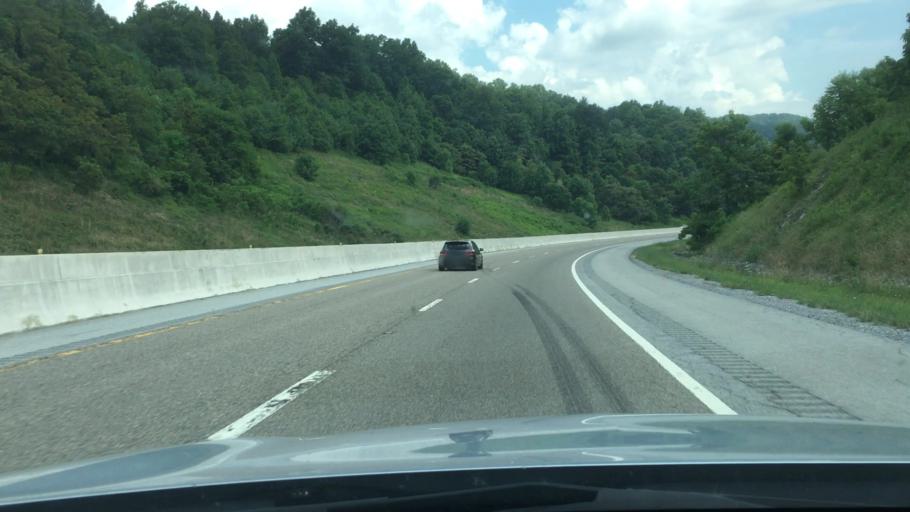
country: US
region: North Carolina
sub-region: Madison County
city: Mars Hill
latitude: 35.9955
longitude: -82.5440
